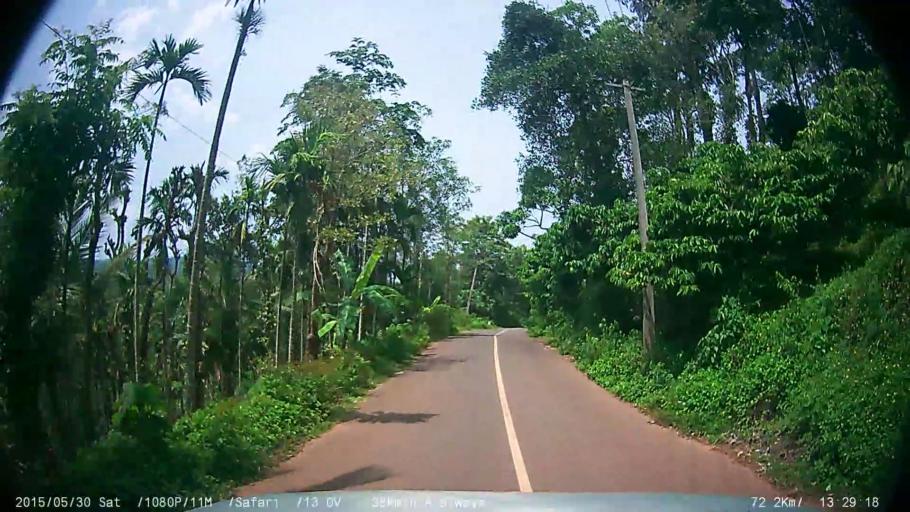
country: IN
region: Kerala
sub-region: Wayanad
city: Panamaram
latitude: 11.8187
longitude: 76.0842
